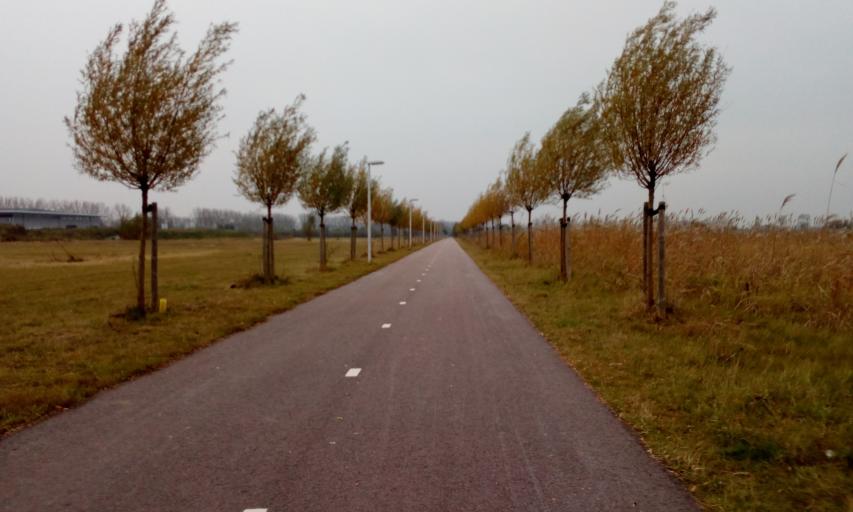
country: NL
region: South Holland
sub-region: Gemeente Lansingerland
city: Bergschenhoek
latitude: 51.9811
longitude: 4.4891
